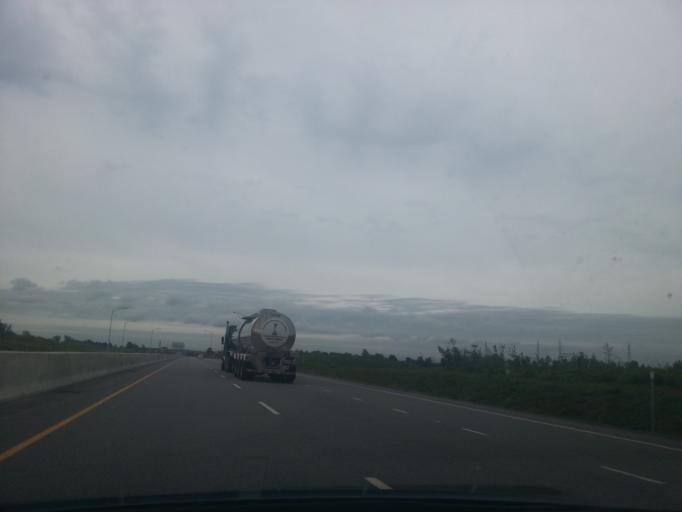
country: CA
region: Quebec
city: Les Cedres
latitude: 45.3331
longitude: -74.0344
